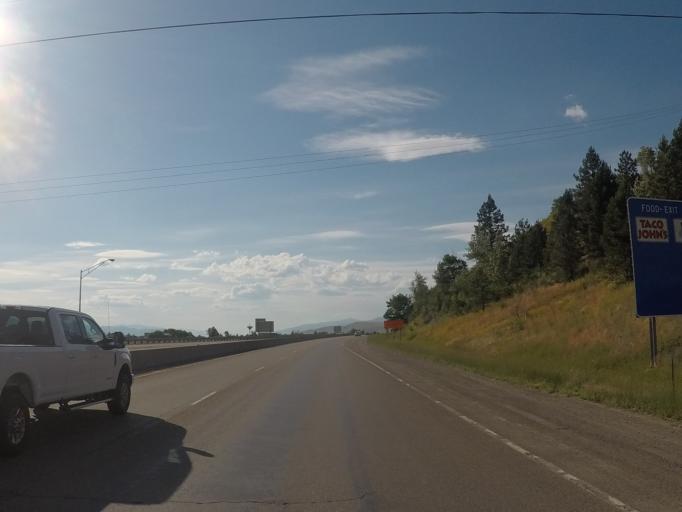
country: US
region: Montana
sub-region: Missoula County
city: Missoula
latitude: 46.8728
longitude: -113.9844
